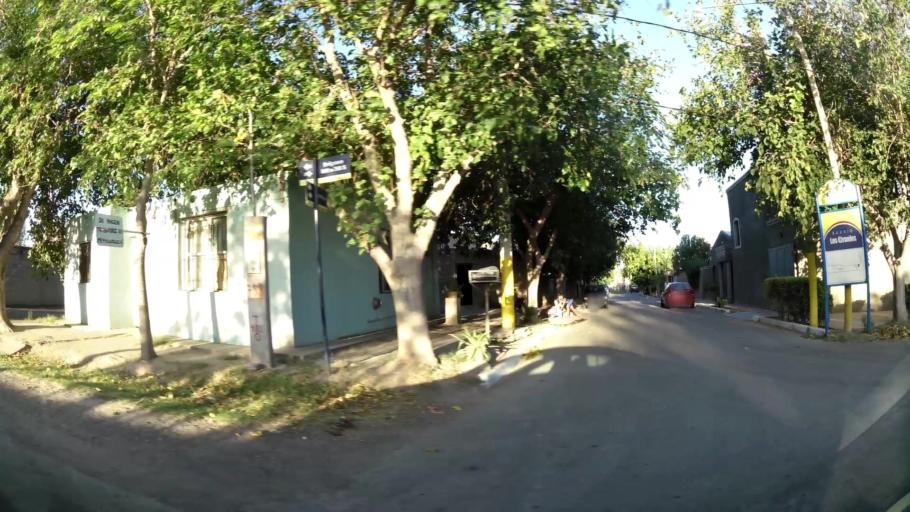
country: AR
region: San Juan
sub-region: Departamento de Santa Lucia
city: Santa Lucia
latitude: -31.5527
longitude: -68.4758
